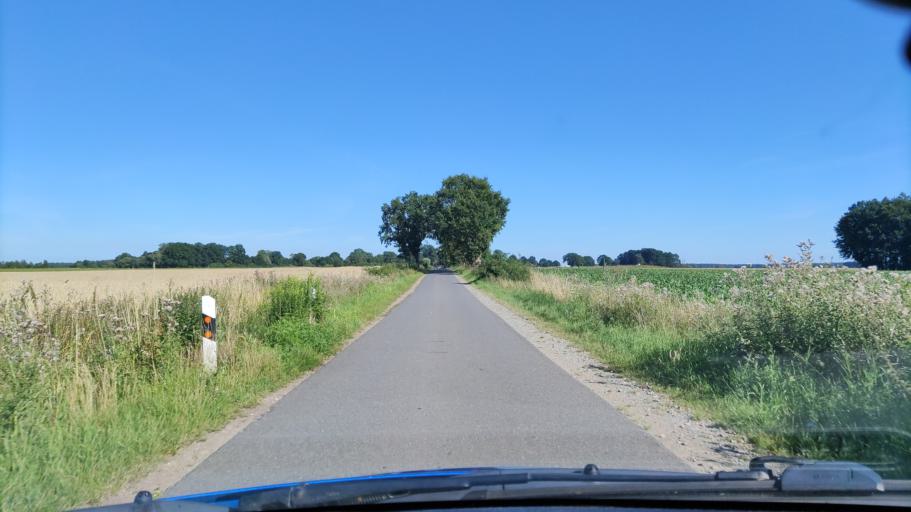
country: DE
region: Lower Saxony
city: Nahrendorf
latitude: 53.1777
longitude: 10.8005
